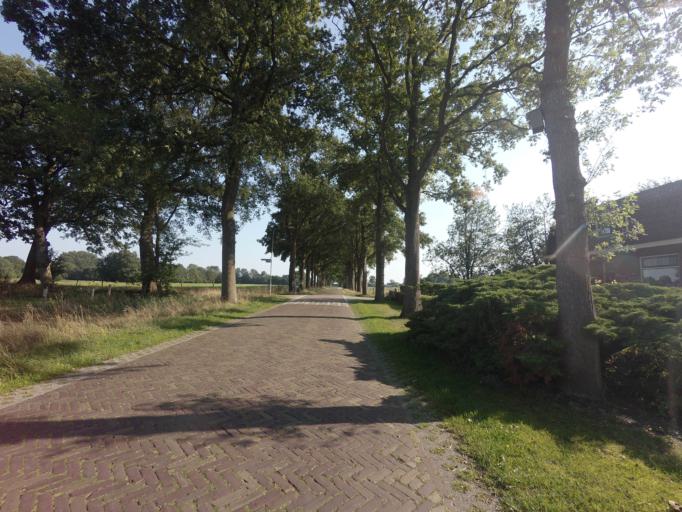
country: NL
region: Groningen
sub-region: Gemeente Zuidhorn
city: Aduard
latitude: 53.1726
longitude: 6.4764
